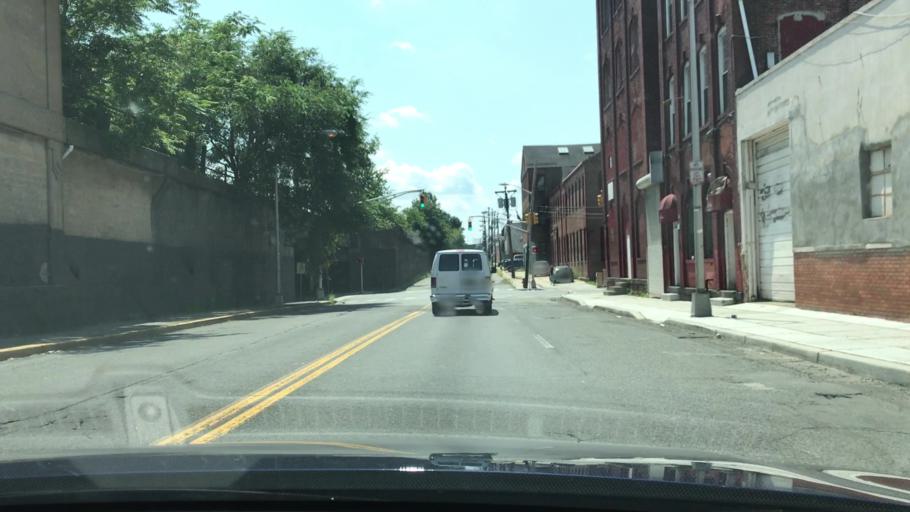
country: US
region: New Jersey
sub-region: Passaic County
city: Paterson
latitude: 40.9136
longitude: -74.1679
